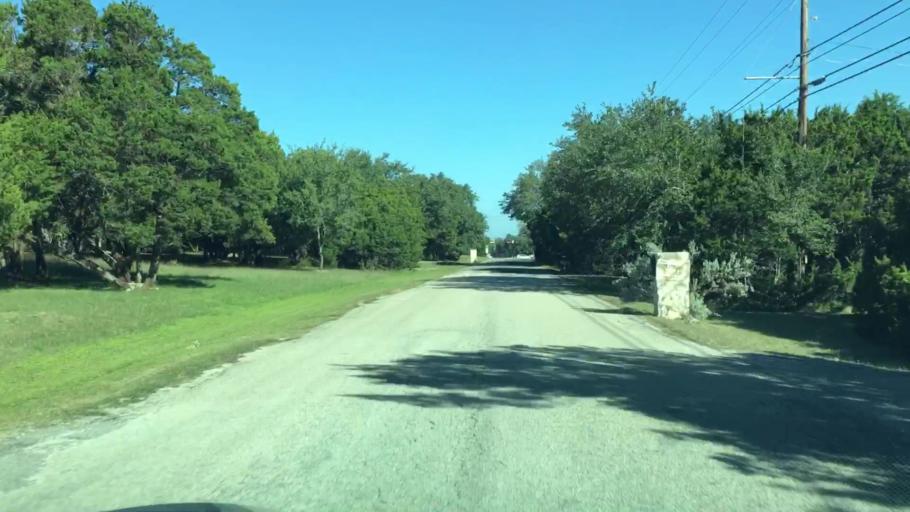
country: US
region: Texas
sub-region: Hays County
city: Dripping Springs
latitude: 30.1949
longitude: -98.0195
